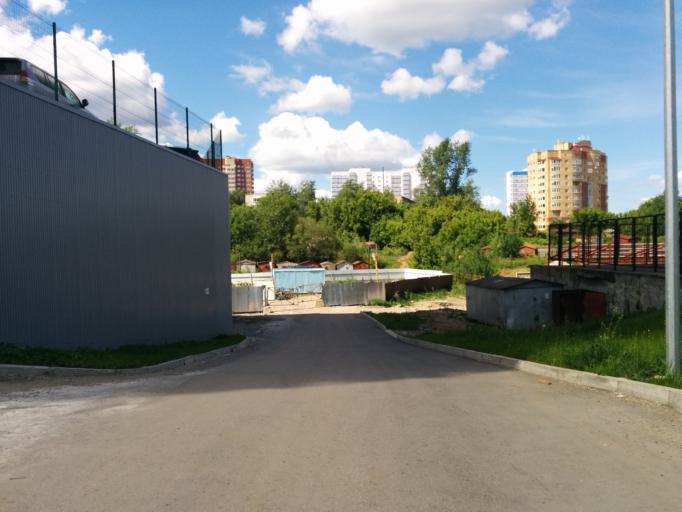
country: RU
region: Perm
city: Perm
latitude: 58.0111
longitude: 56.3032
